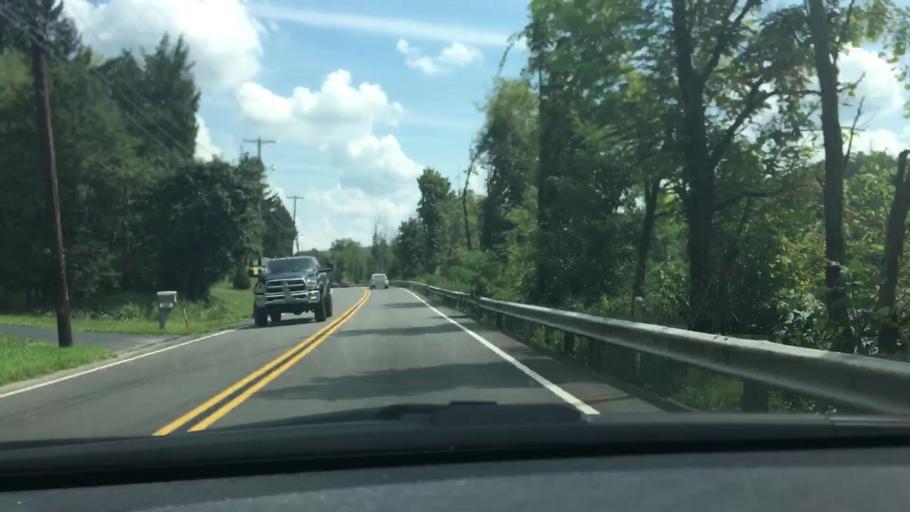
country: US
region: Pennsylvania
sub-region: Washington County
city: Thompsonville
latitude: 40.2565
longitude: -80.1299
